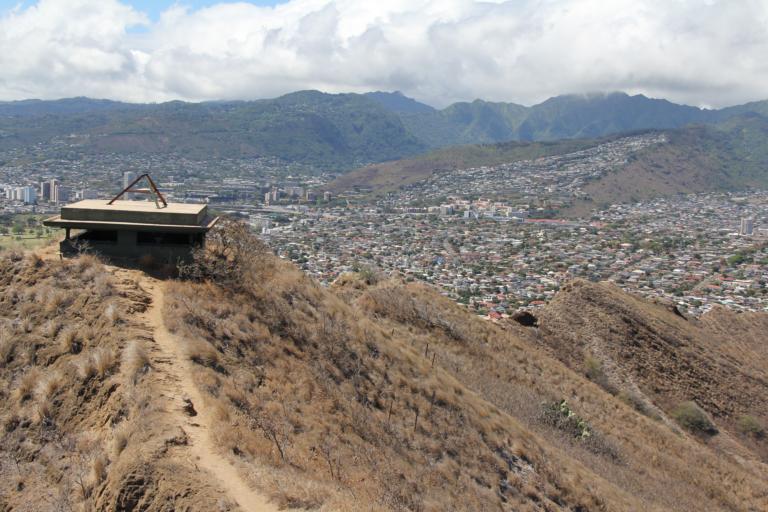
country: US
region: Hawaii
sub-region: Honolulu County
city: Honolulu
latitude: 21.2598
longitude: -157.8118
